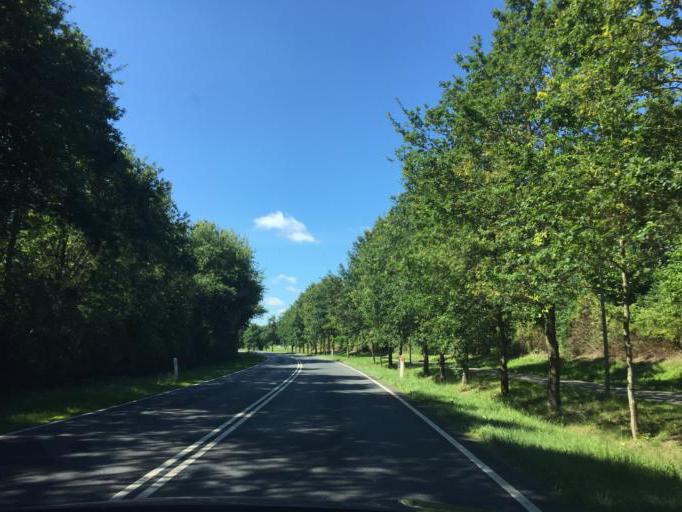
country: DK
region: South Denmark
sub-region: Odense Kommune
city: Bellinge
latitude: 55.3734
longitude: 10.3303
